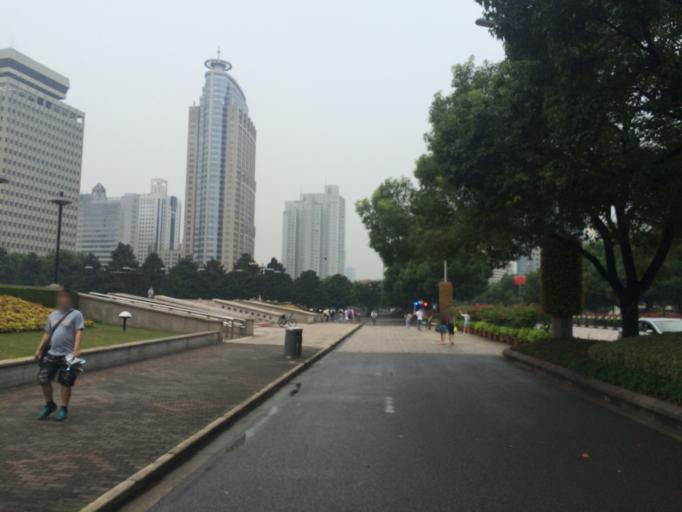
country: CN
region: Shanghai Shi
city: Shanghai
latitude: 31.2319
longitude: 121.4701
